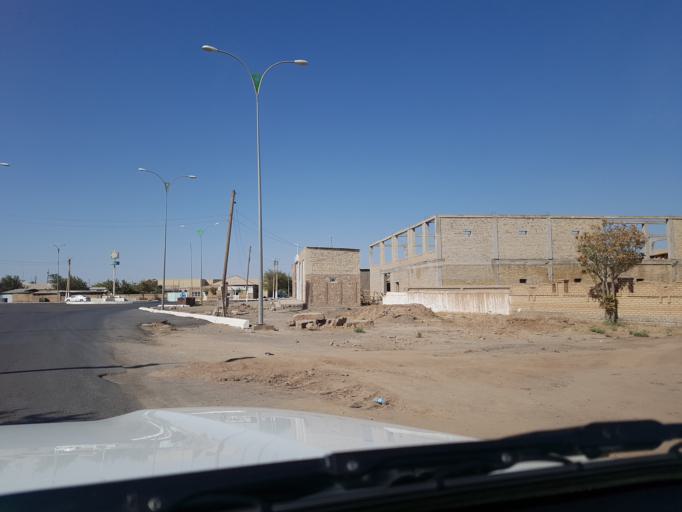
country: IR
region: Razavi Khorasan
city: Sarakhs
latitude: 36.5227
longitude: 61.2173
